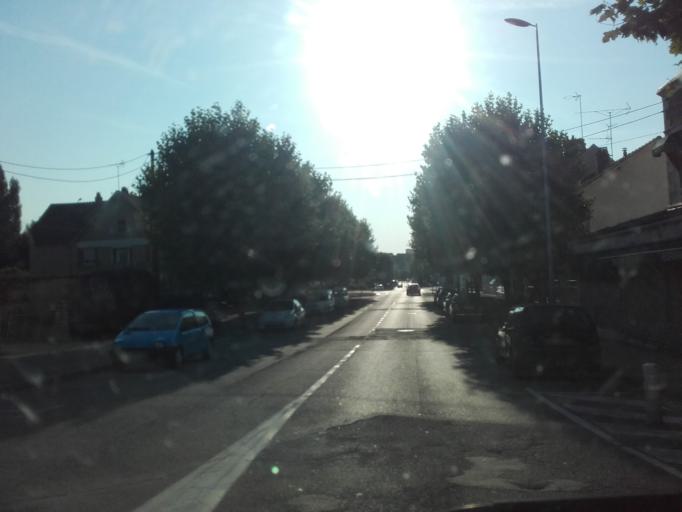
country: FR
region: Bourgogne
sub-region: Departement de l'Yonne
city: Auxerre
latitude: 47.7961
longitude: 3.5840
